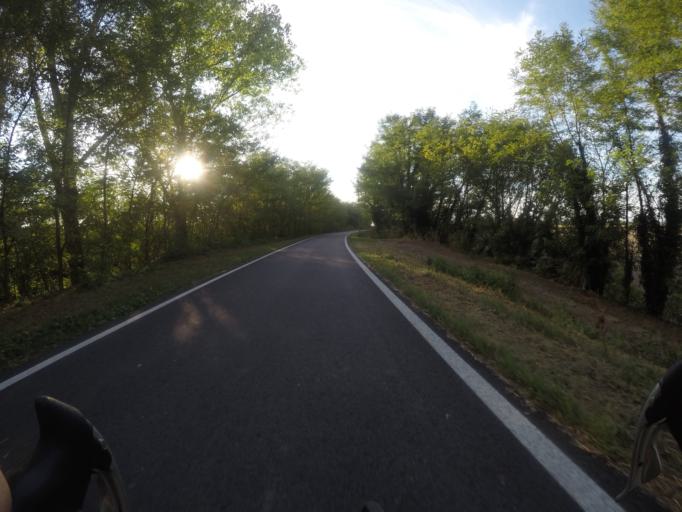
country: IT
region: Veneto
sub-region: Provincia di Rovigo
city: Pincara
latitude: 44.9963
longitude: 11.5895
